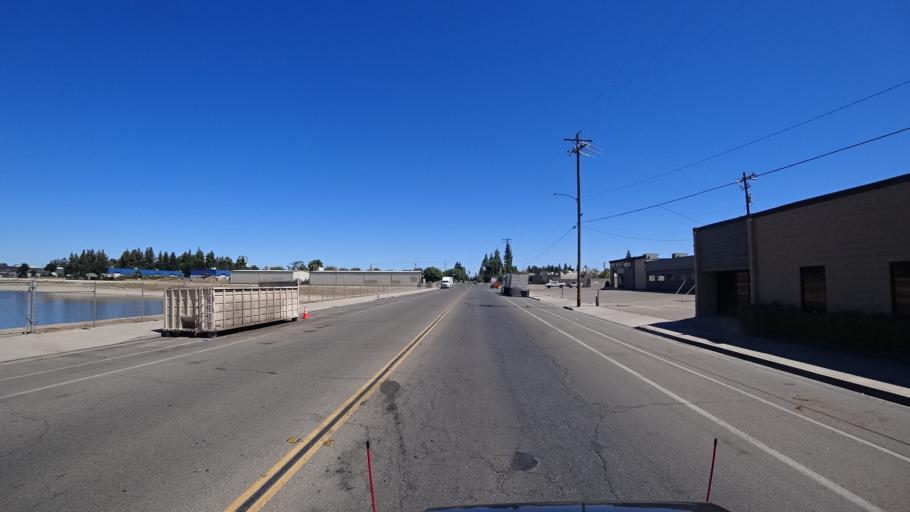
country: US
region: California
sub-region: Fresno County
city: West Park
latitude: 36.7916
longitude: -119.8533
